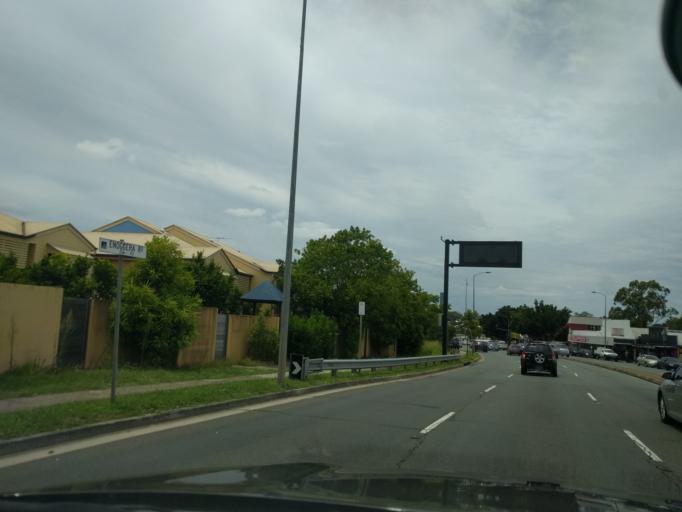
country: AU
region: Queensland
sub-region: Brisbane
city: Wilston
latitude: -27.4354
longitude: 153.0063
